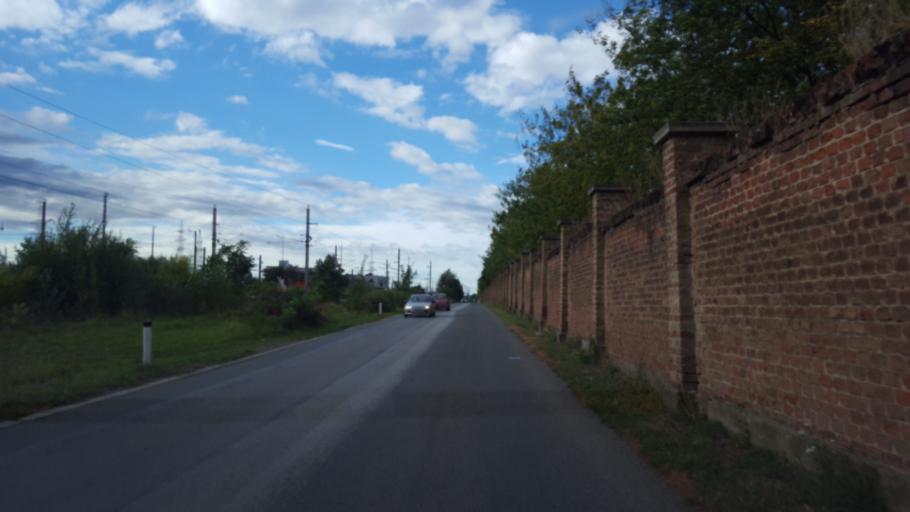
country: AT
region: Lower Austria
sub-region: Politischer Bezirk Wien-Umgebung
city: Schwechat
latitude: 48.1480
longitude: 16.4302
